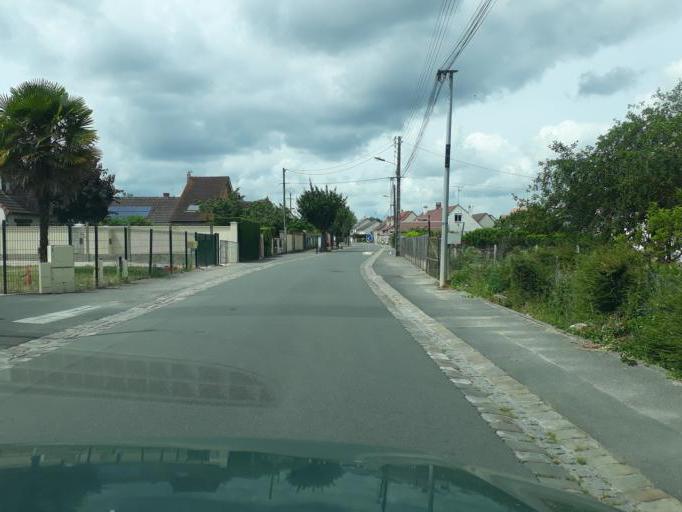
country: FR
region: Centre
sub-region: Departement du Loiret
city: La Chapelle-Saint-Mesmin
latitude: 47.8975
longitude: 1.8252
